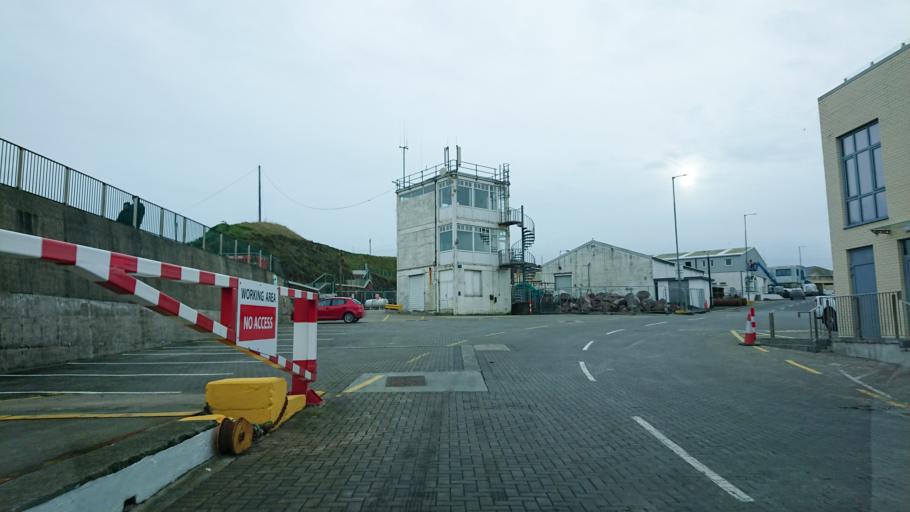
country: IE
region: Munster
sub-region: Waterford
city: Dunmore East
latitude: 52.1471
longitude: -6.9905
